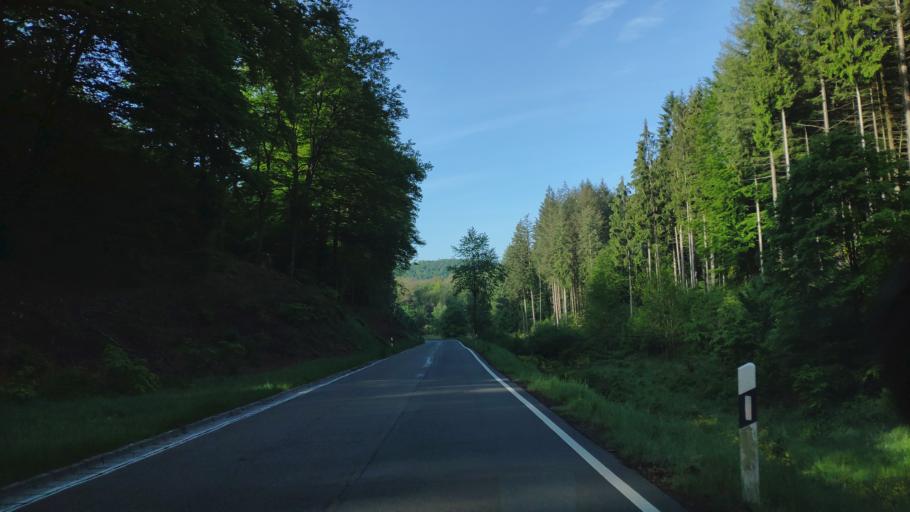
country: DE
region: Rheinland-Pfalz
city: Ludwigswinkel
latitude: 49.1120
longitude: 7.6716
